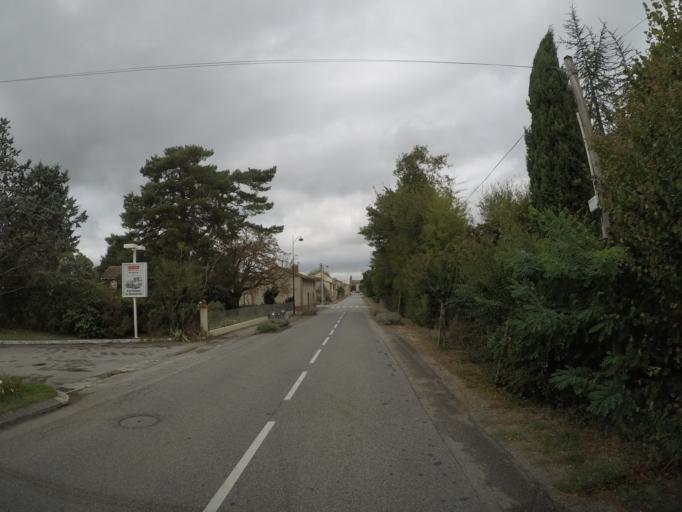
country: FR
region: Midi-Pyrenees
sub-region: Departement de la Haute-Garonne
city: Gaillac-Toulza
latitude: 43.1717
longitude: 1.4106
